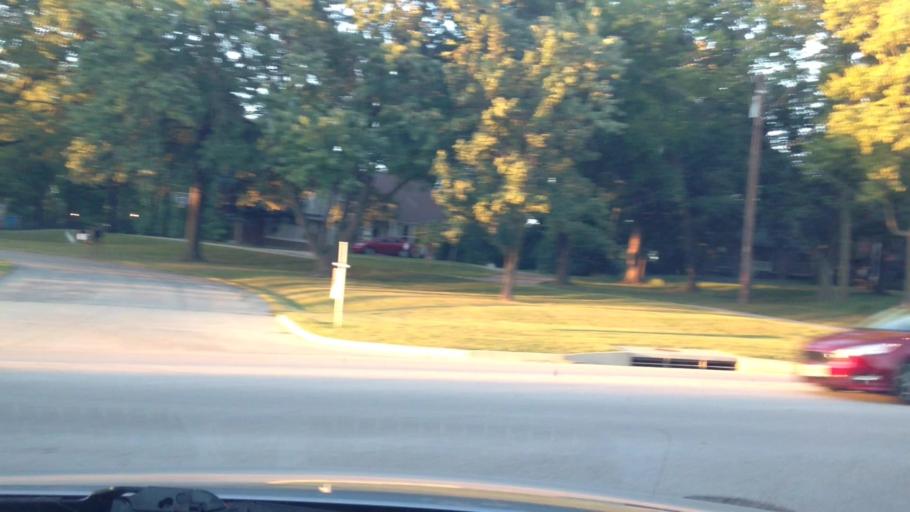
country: US
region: Missouri
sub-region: Platte County
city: Parkville
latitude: 39.2250
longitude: -94.6578
